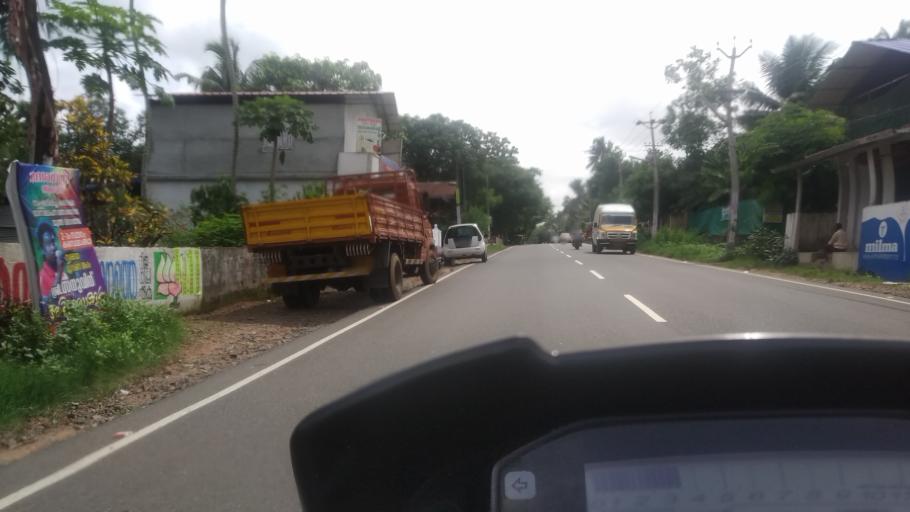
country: IN
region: Kerala
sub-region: Ernakulam
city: Aluva
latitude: 10.1265
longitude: 76.3274
